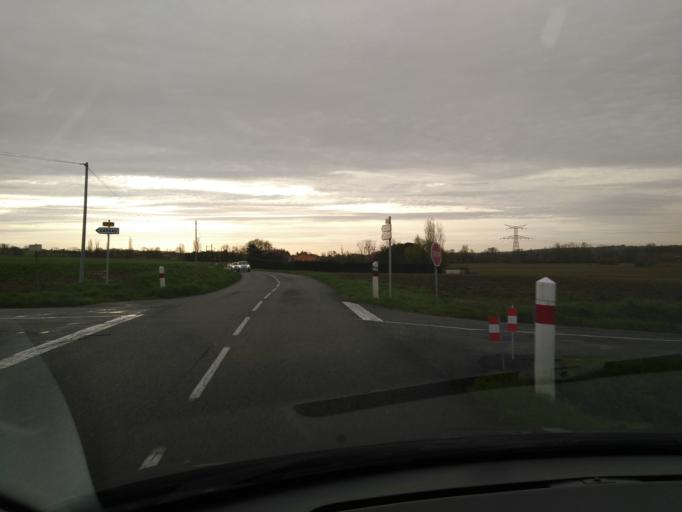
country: FR
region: Midi-Pyrenees
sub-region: Departement de la Haute-Garonne
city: Labastide-Saint-Sernin
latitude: 43.7524
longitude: 1.4606
